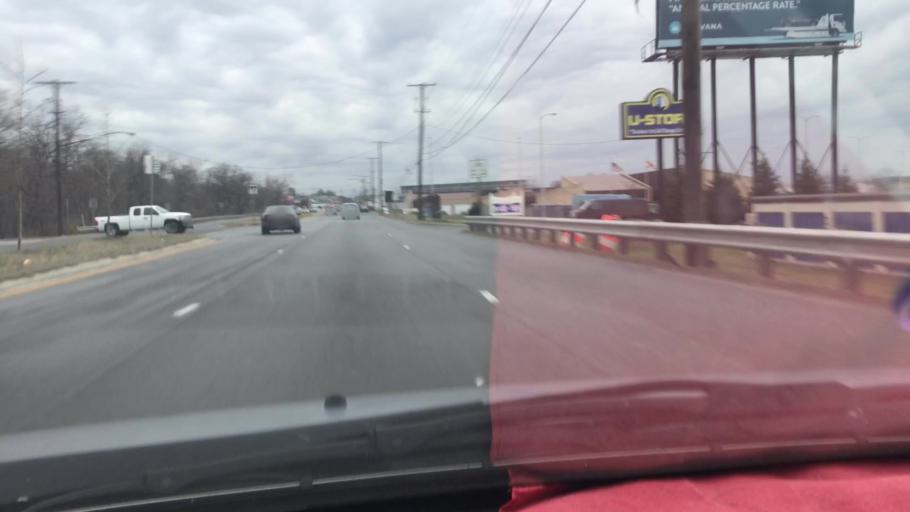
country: US
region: Maryland
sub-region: Prince George's County
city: Bladensburg
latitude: 38.9360
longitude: -76.9364
